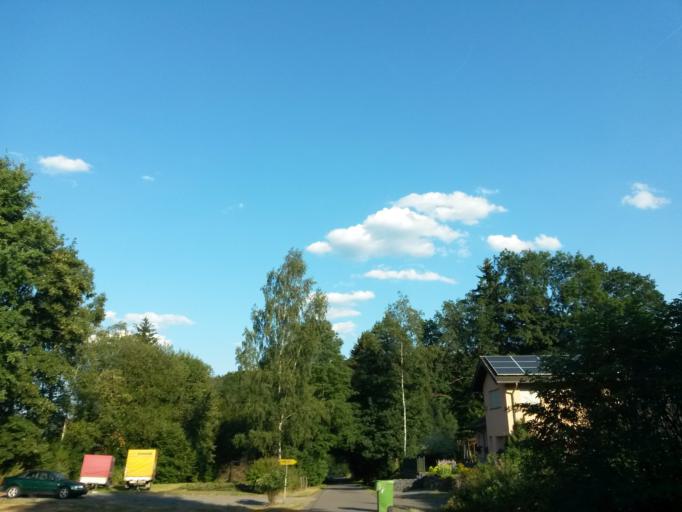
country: DE
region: North Rhine-Westphalia
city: Meinerzhagen
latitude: 51.1082
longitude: 7.7065
